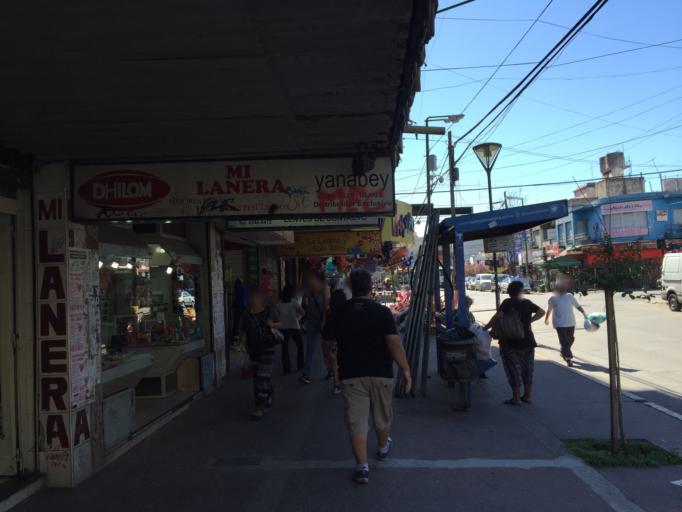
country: AR
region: Buenos Aires
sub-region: Partido de Lomas de Zamora
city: Lomas de Zamora
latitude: -34.7594
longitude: -58.4005
